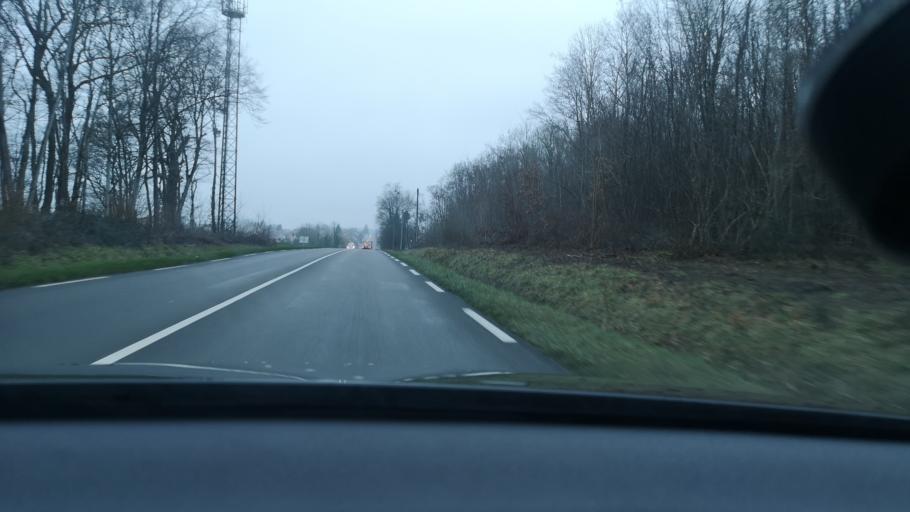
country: FR
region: Bourgogne
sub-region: Departement de la Cote-d'Or
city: Fenay
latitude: 47.1631
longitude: 5.0846
